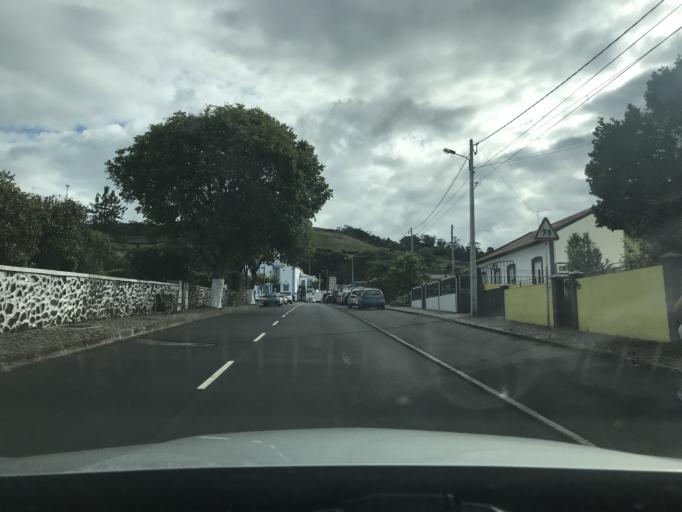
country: PT
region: Azores
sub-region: Angra do Heroismo
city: Angra do Heroismo
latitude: 38.6732
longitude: -27.2500
